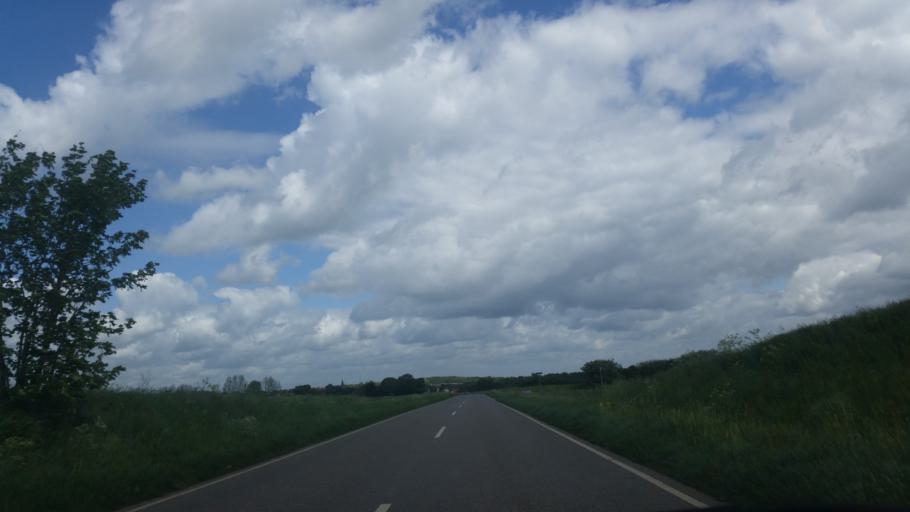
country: DK
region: South Denmark
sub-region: Kolding Kommune
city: Christiansfeld
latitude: 55.3426
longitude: 9.4697
